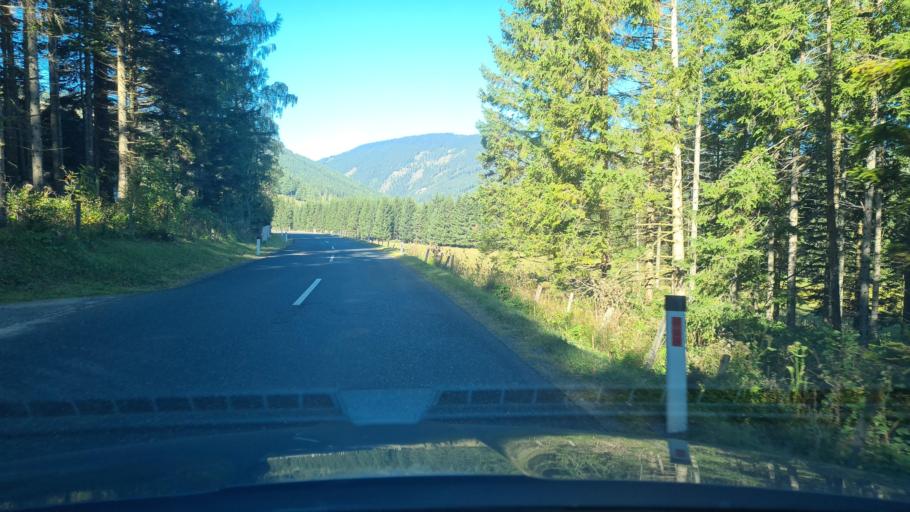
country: AT
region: Styria
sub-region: Politischer Bezirk Weiz
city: Passail
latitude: 47.3446
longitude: 15.4741
